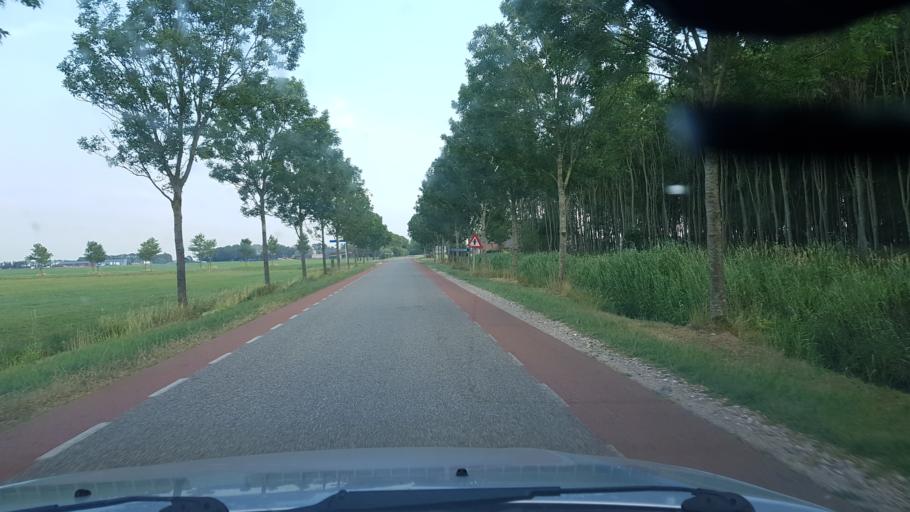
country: NL
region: Friesland
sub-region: Gemeente Ferwerderadiel
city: Burdaard
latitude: 53.3053
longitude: 5.8727
